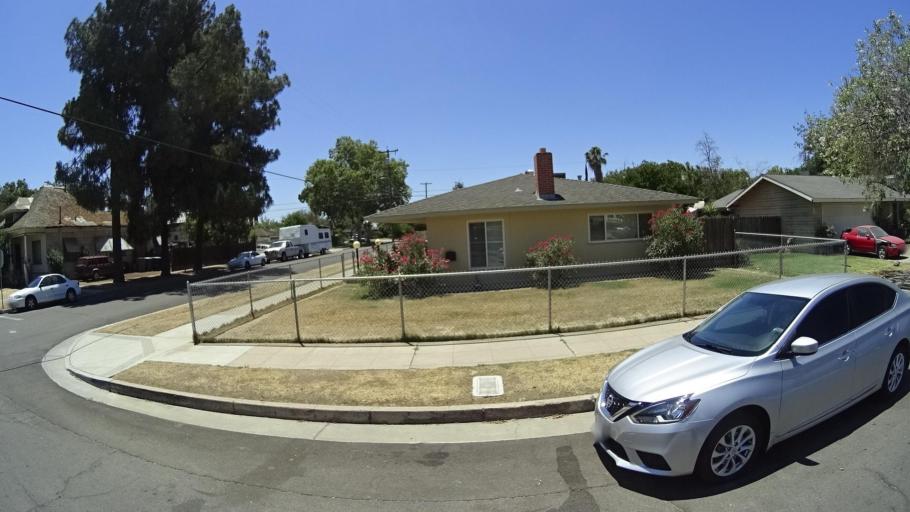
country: US
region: California
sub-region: Fresno County
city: Fresno
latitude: 36.7823
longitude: -119.7930
